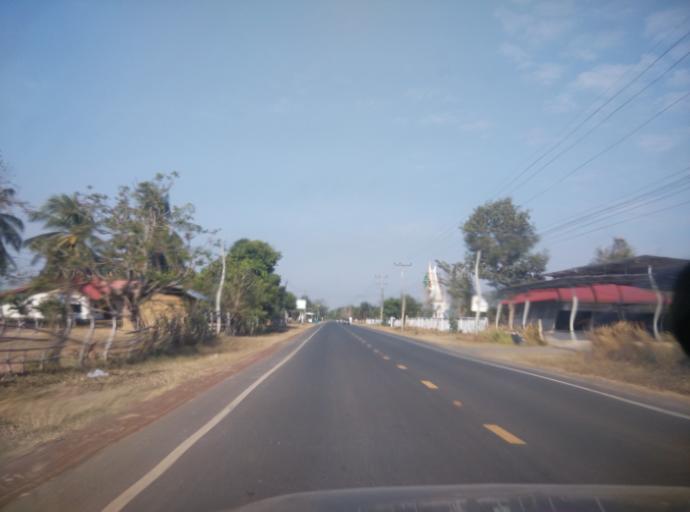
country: TH
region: Sisaket
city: Si Sa Ket
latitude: 15.1153
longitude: 104.2631
